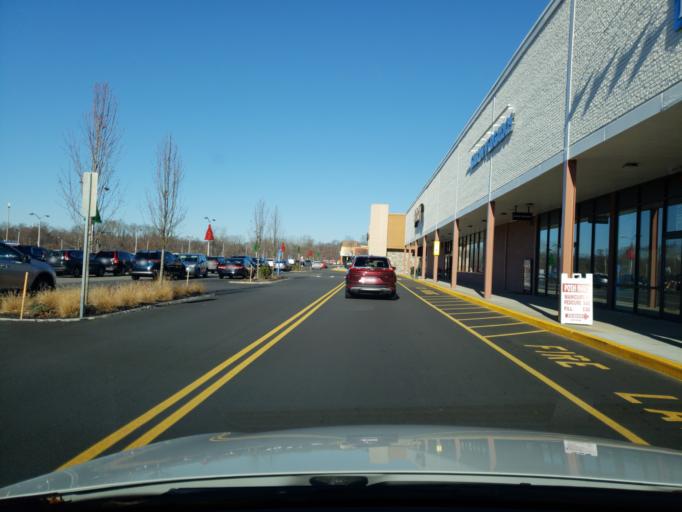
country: US
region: Massachusetts
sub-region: Essex County
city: North Andover
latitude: 42.6827
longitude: -71.1353
